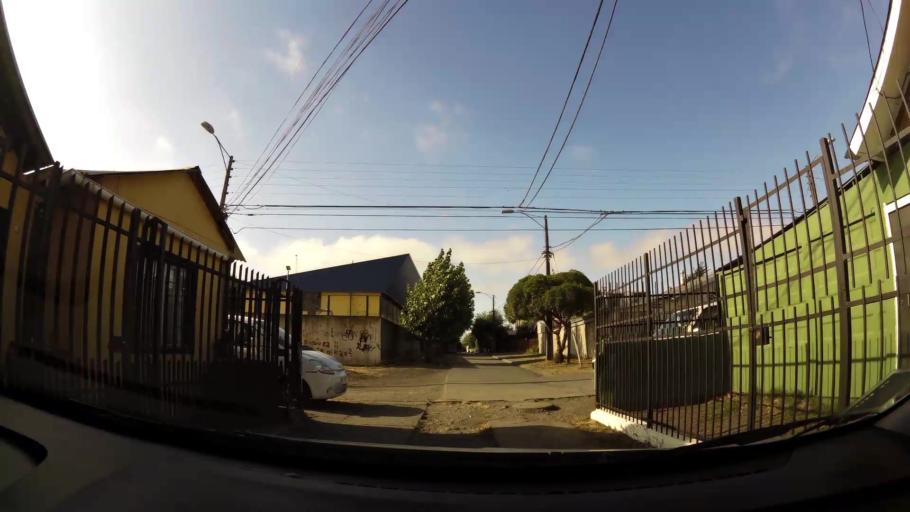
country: CL
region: Biobio
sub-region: Provincia de Concepcion
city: Concepcion
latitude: -36.7928
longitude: -73.0990
